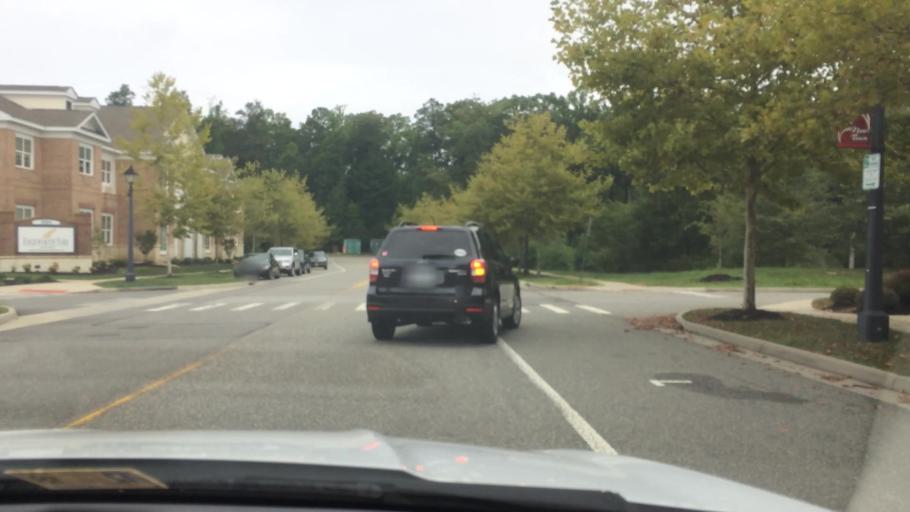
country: US
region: Virginia
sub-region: James City County
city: Williamsburg
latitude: 37.2844
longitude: -76.7434
